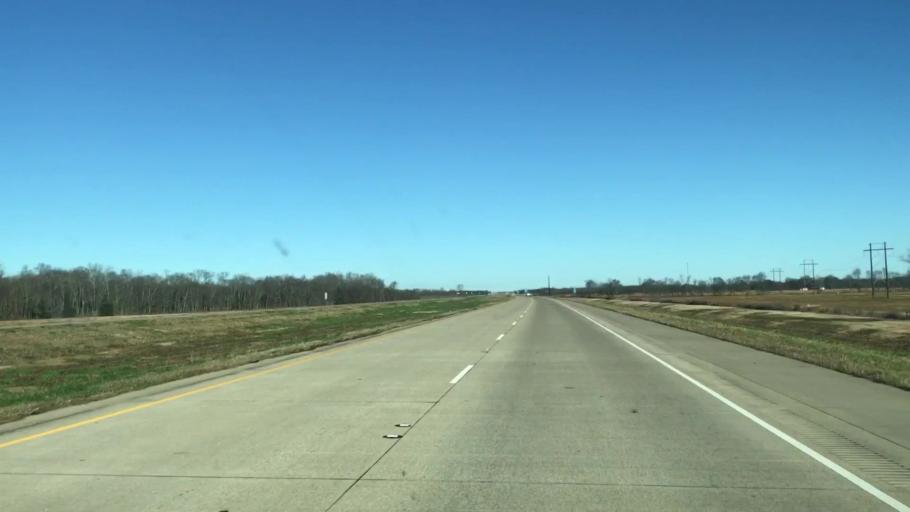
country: US
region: Louisiana
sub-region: Caddo Parish
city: Blanchard
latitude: 32.6556
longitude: -93.8422
